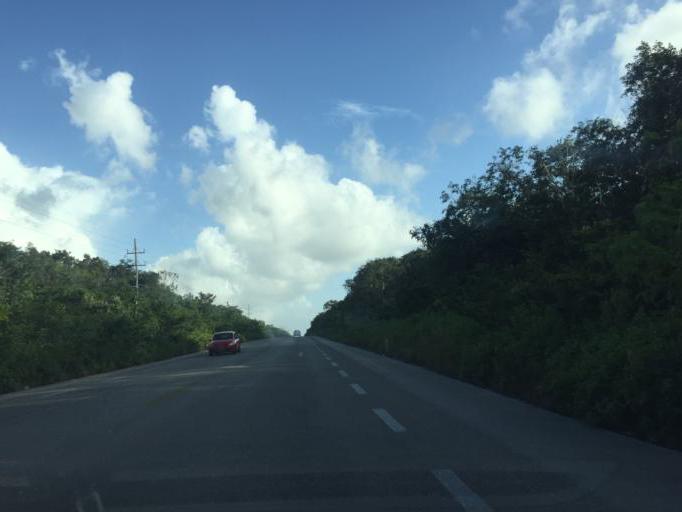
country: MX
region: Quintana Roo
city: Coba
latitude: 20.4836
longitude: -87.6977
